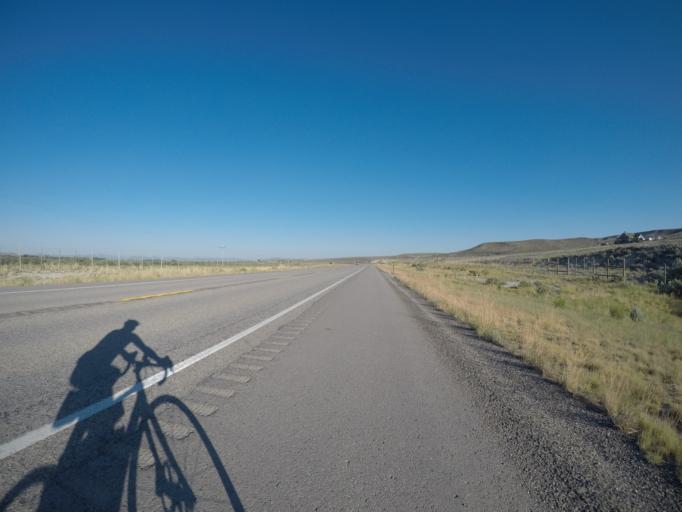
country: US
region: Wyoming
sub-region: Sublette County
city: Pinedale
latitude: 42.8847
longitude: -110.0034
